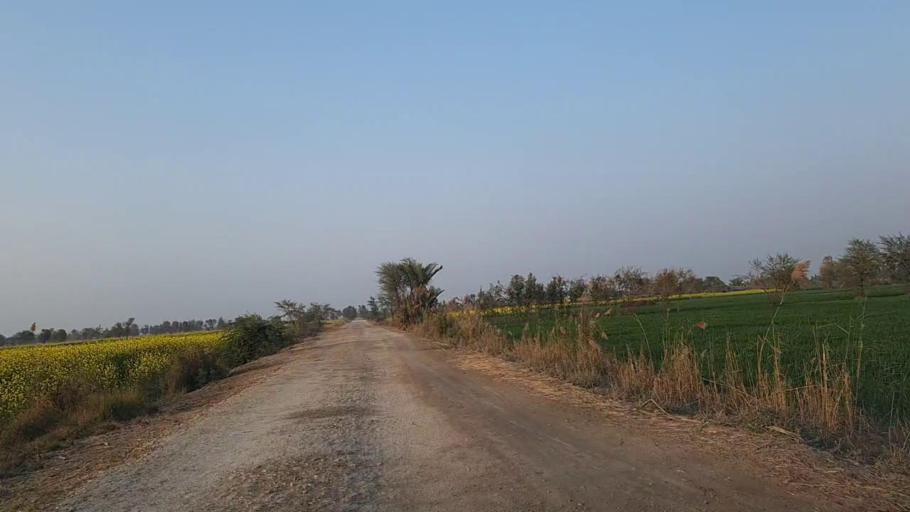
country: PK
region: Sindh
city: Daur
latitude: 26.4256
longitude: 68.3859
